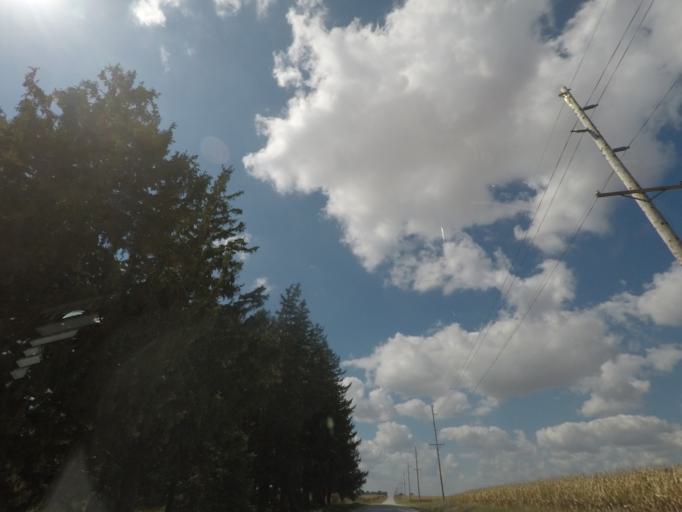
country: US
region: Iowa
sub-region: Story County
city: Nevada
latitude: 42.0344
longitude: -93.3956
